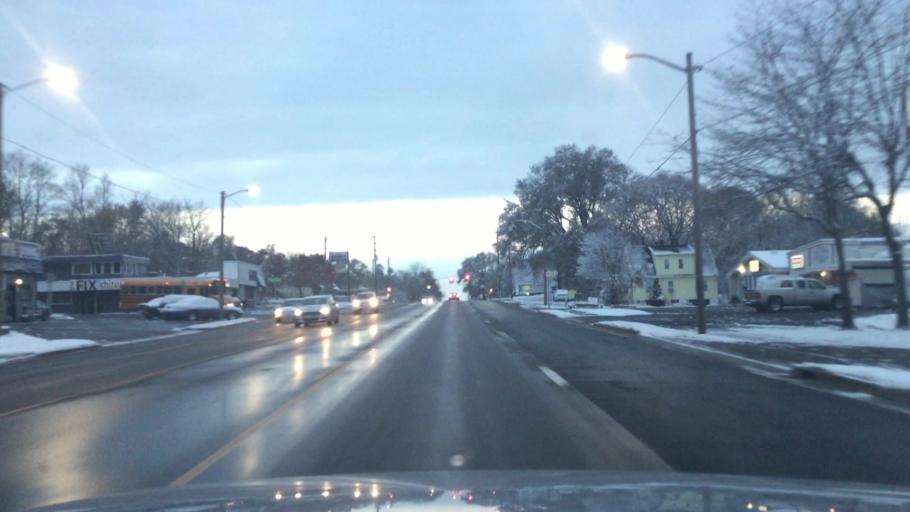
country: US
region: Michigan
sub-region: Oakland County
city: Keego Harbor
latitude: 42.6392
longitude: -83.3601
